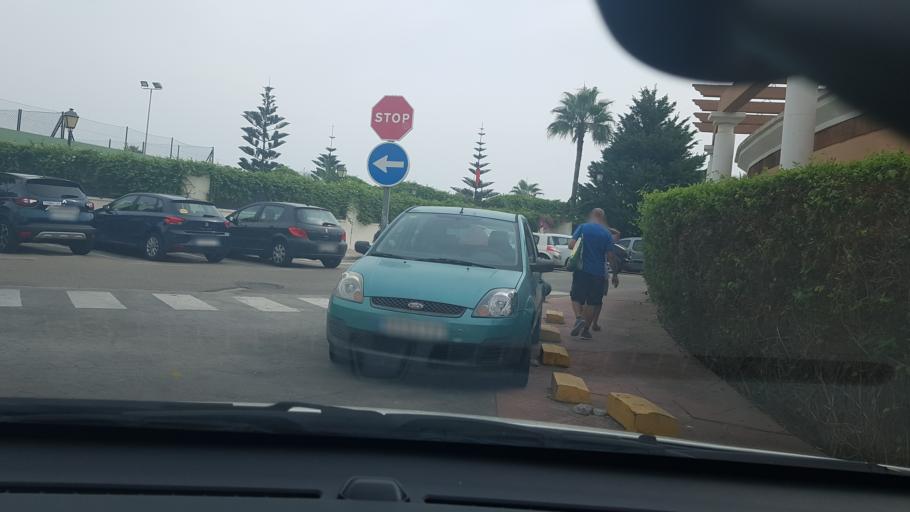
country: ES
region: Andalusia
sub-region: Provincia de Malaga
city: Manilva
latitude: 36.3704
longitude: -5.2247
